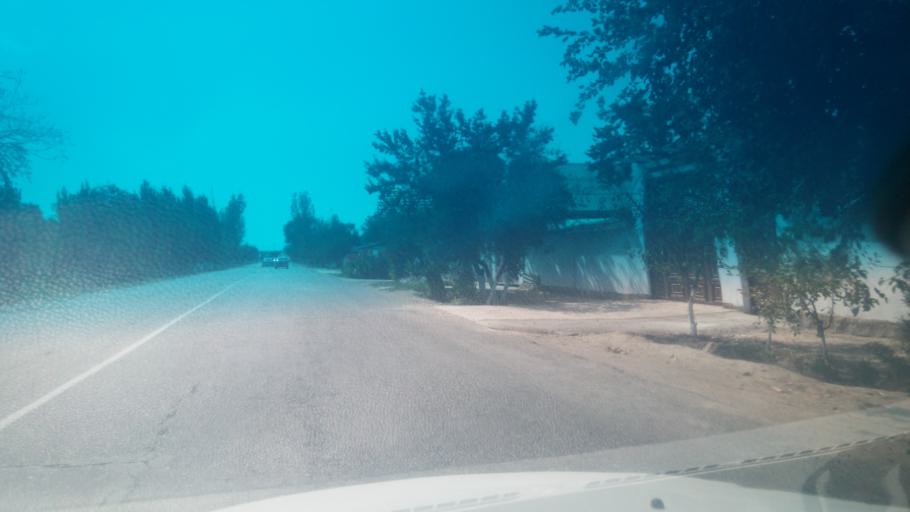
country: UZ
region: Sirdaryo
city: Sirdaryo
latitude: 40.8112
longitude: 68.6755
